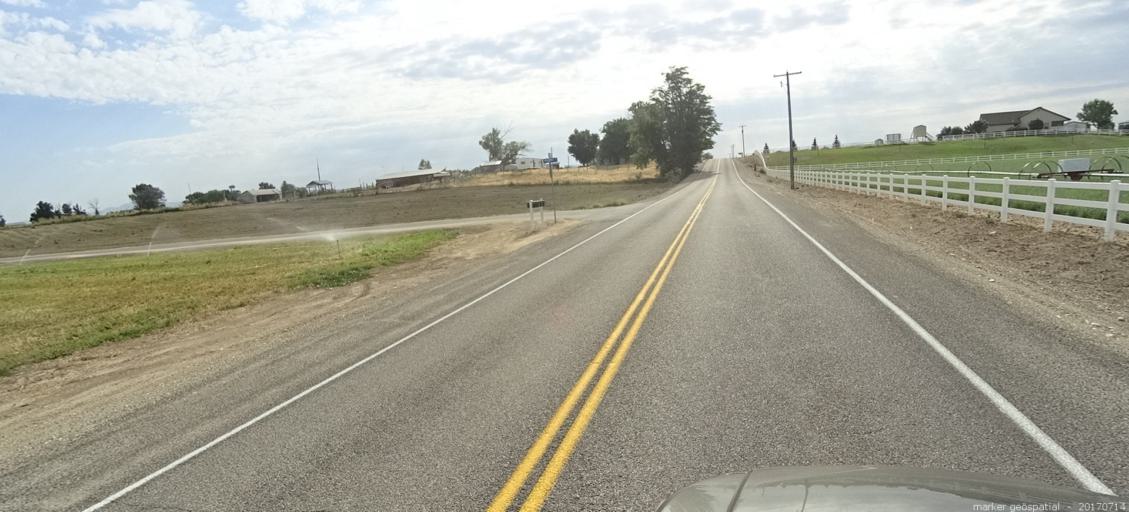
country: US
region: Idaho
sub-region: Ada County
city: Kuna
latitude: 43.4737
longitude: -116.3684
